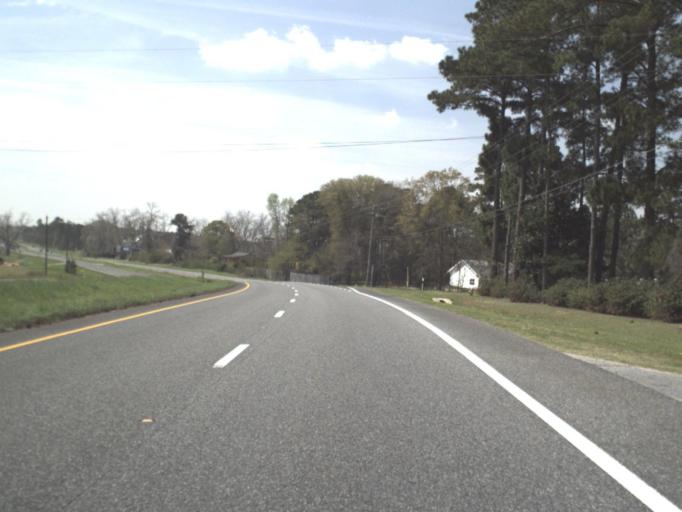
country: US
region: Florida
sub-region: Gadsden County
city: Havana
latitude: 30.6661
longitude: -84.4083
